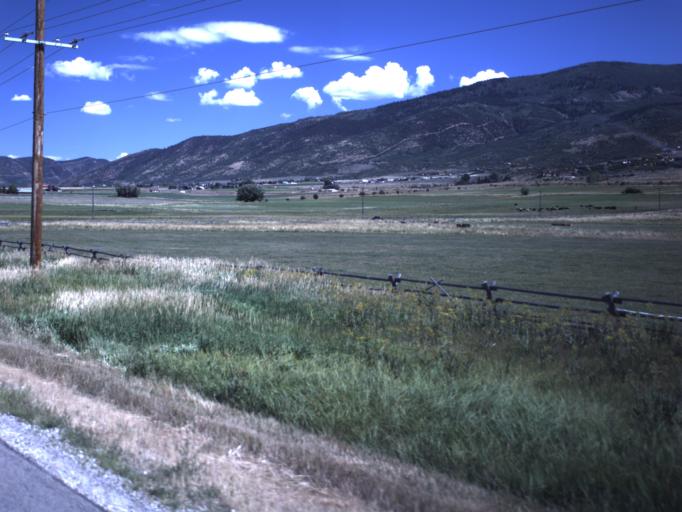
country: US
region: Utah
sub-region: Summit County
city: Kamas
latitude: 40.6640
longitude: -111.2808
